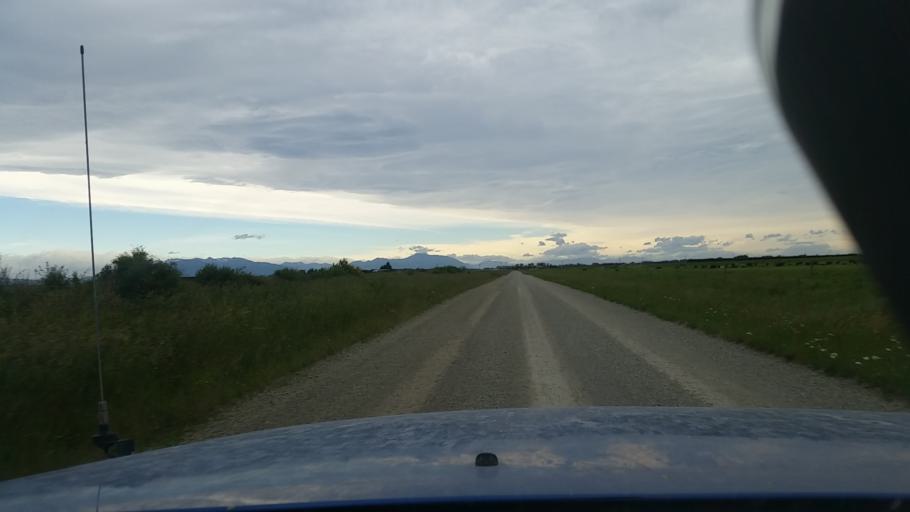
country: NZ
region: Canterbury
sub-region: Ashburton District
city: Tinwald
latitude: -43.9824
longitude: 171.5070
